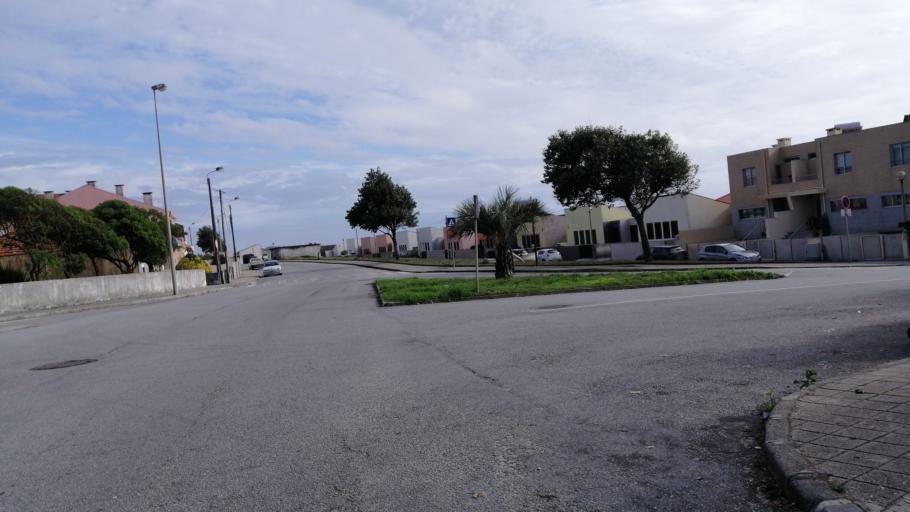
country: PT
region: Porto
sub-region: Matosinhos
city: Lavra
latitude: 41.2644
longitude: -8.7240
